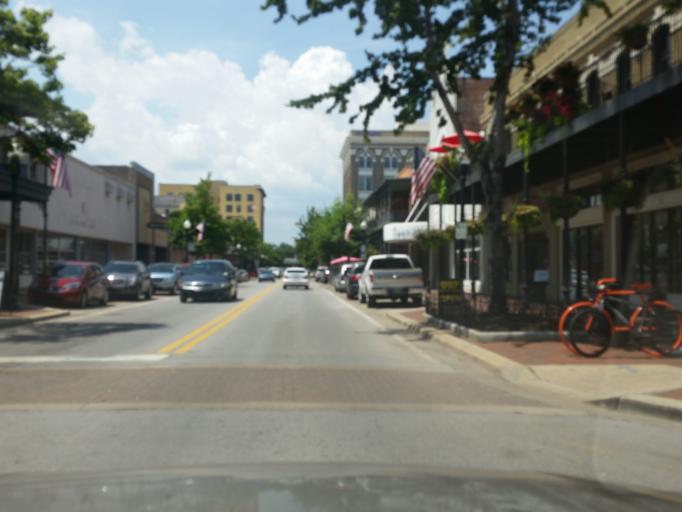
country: US
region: Florida
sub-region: Escambia County
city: Pensacola
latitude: 30.4103
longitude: -87.2148
